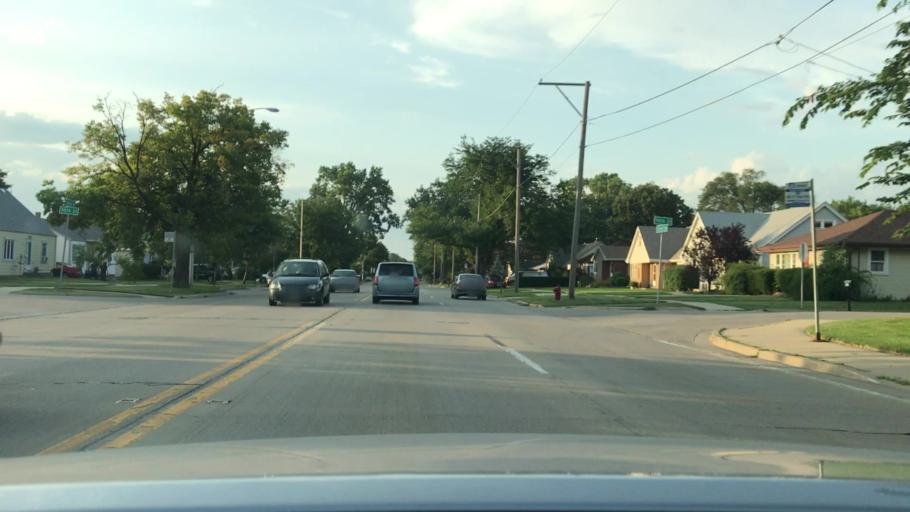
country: US
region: Illinois
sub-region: Cook County
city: Oak Lawn
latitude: 41.7286
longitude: -87.7606
